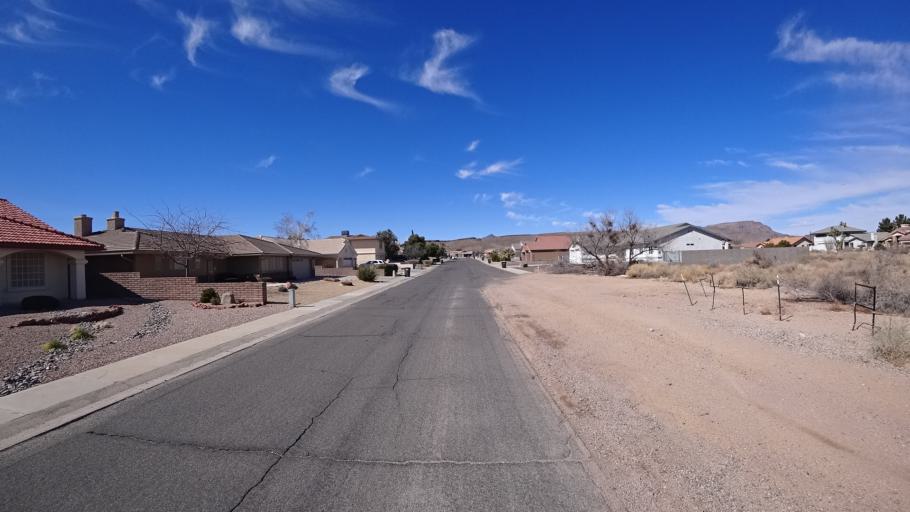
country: US
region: Arizona
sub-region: Mohave County
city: Kingman
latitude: 35.2117
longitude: -114.0428
